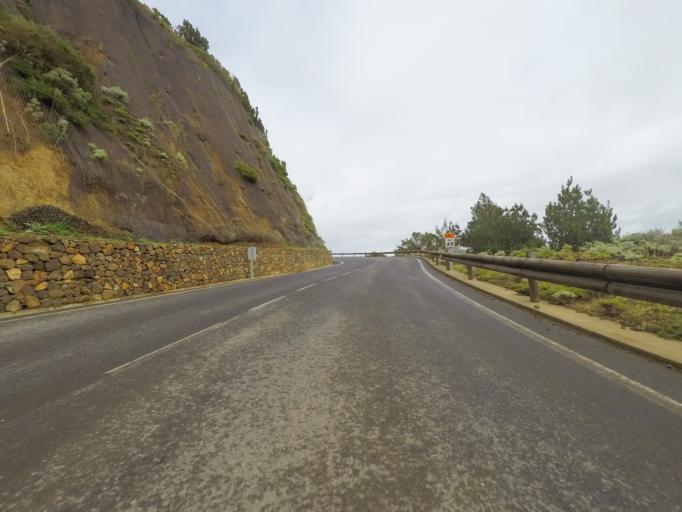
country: ES
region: Canary Islands
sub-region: Provincia de Santa Cruz de Tenerife
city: Vallehermosa
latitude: 28.1627
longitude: -17.2897
